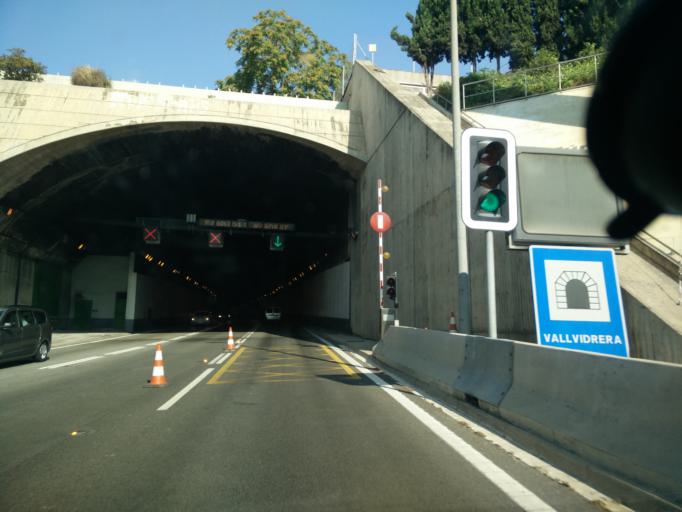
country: ES
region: Catalonia
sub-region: Provincia de Barcelona
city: les Corts
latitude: 41.4064
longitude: 2.1155
